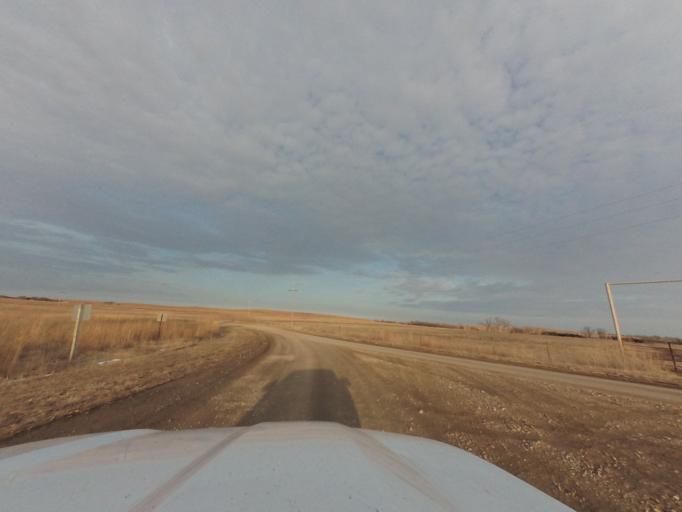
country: US
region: Kansas
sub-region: Morris County
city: Council Grove
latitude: 38.5304
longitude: -96.4172
